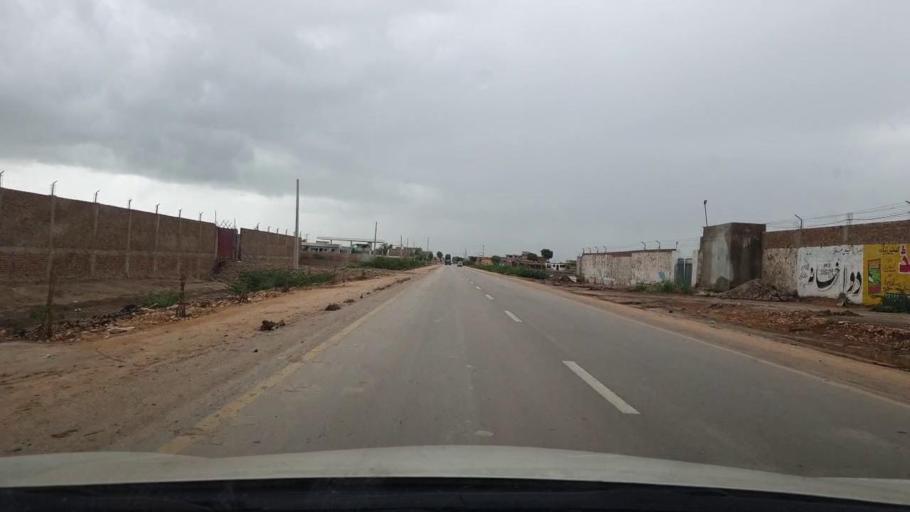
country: PK
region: Sindh
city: Kario
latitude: 24.6529
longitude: 68.5110
